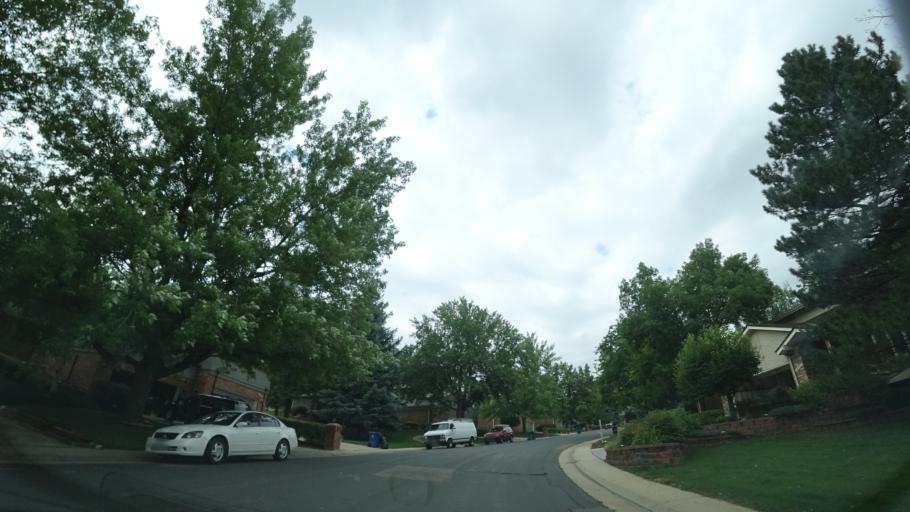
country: US
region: Colorado
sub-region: Jefferson County
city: West Pleasant View
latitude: 39.7200
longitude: -105.1634
